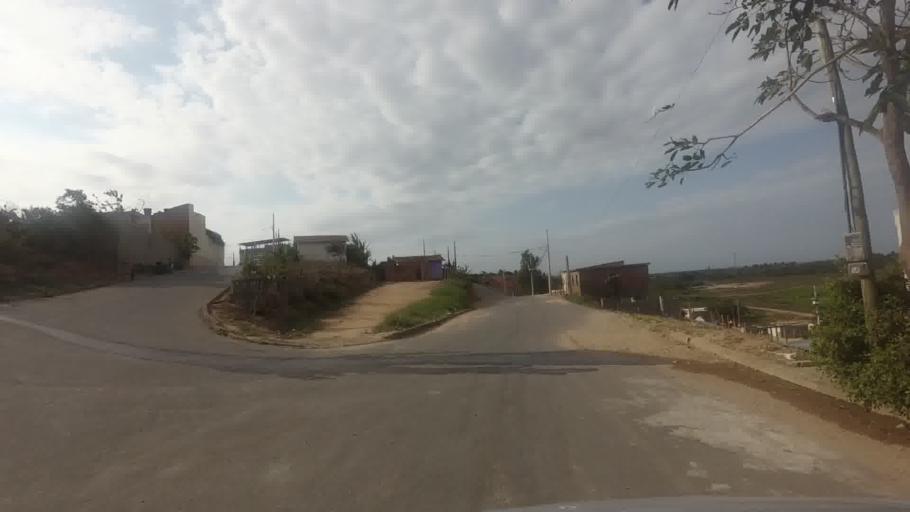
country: BR
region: Espirito Santo
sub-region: Itapemirim
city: Itapemirim
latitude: -21.0156
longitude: -40.8281
